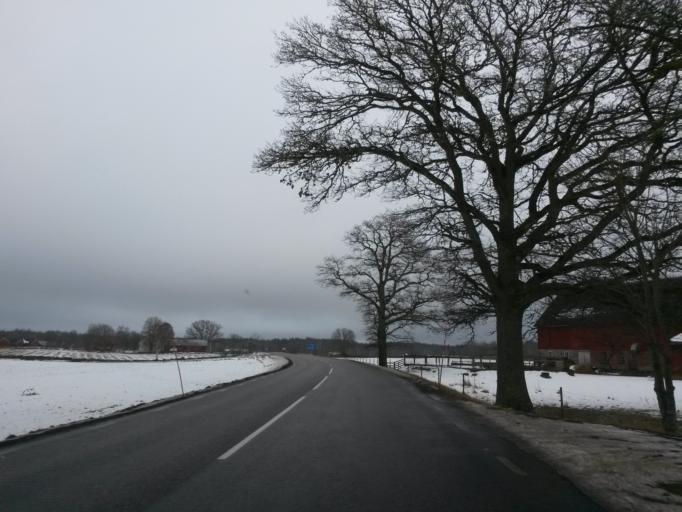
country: SE
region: Vaestra Goetaland
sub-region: Herrljunga Kommun
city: Herrljunga
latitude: 57.9946
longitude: 12.9347
